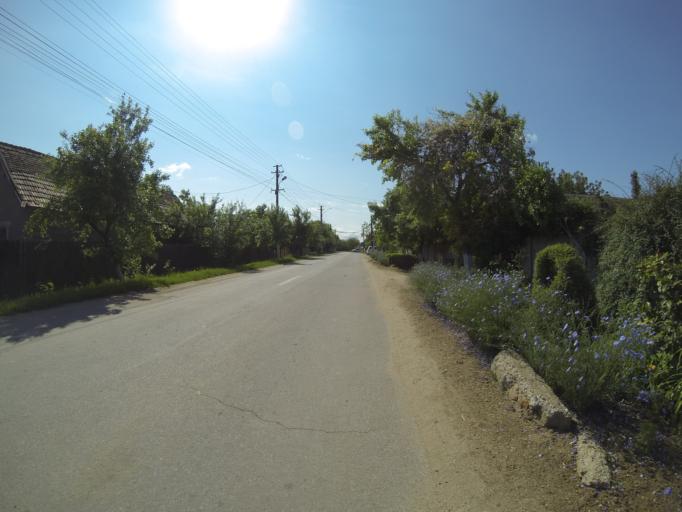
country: RO
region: Dolj
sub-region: Comuna Plenita
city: Plenita
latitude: 44.2218
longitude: 23.1804
